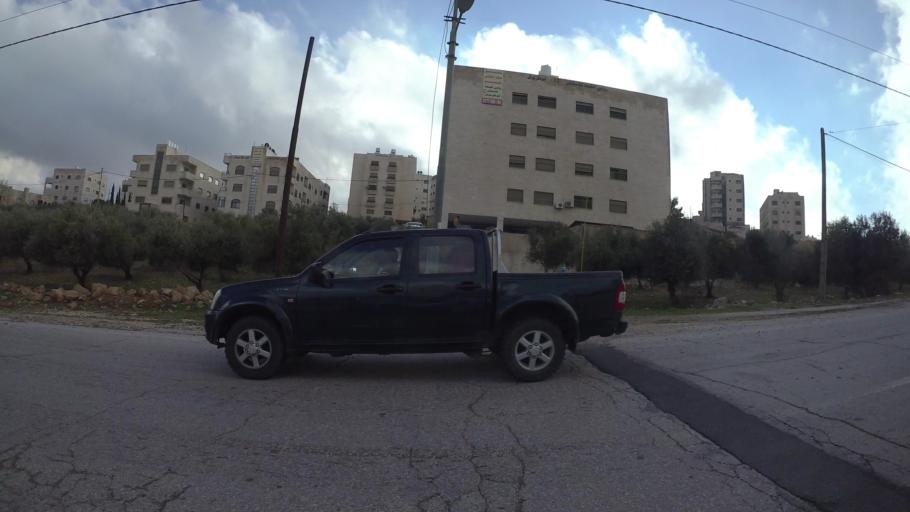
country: JO
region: Amman
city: Al Jubayhah
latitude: 32.0562
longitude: 35.8961
